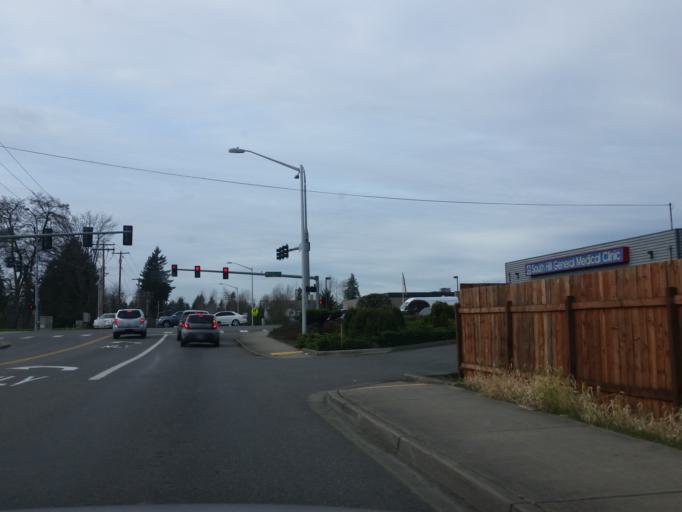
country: US
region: Washington
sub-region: Pierce County
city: South Hill
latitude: 47.1330
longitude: -122.2921
